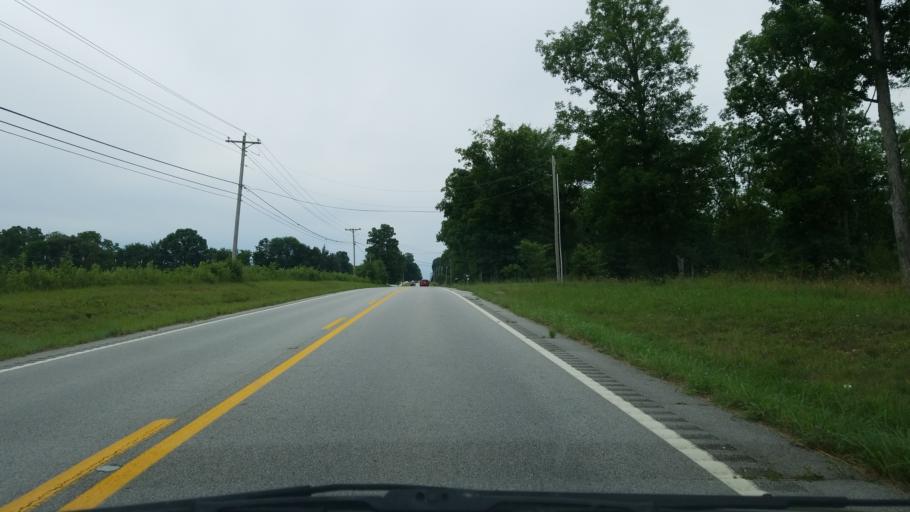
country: US
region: Tennessee
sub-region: Bradley County
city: Hopewell
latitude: 35.2878
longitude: -84.9707
